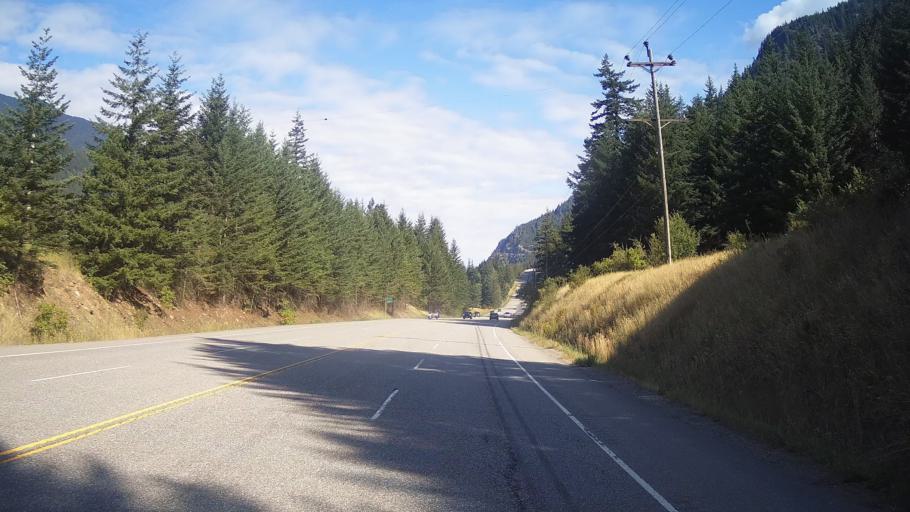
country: CA
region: British Columbia
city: Hope
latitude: 50.0500
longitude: -121.5408
